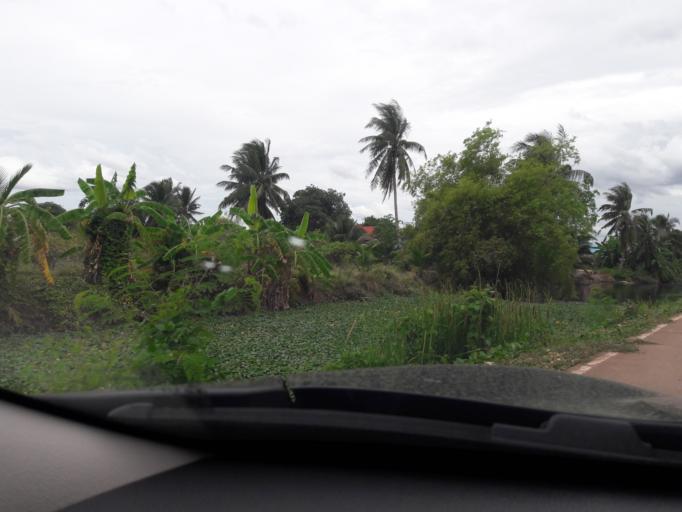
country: TH
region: Ratchaburi
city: Bang Phae
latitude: 13.6090
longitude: 99.9089
